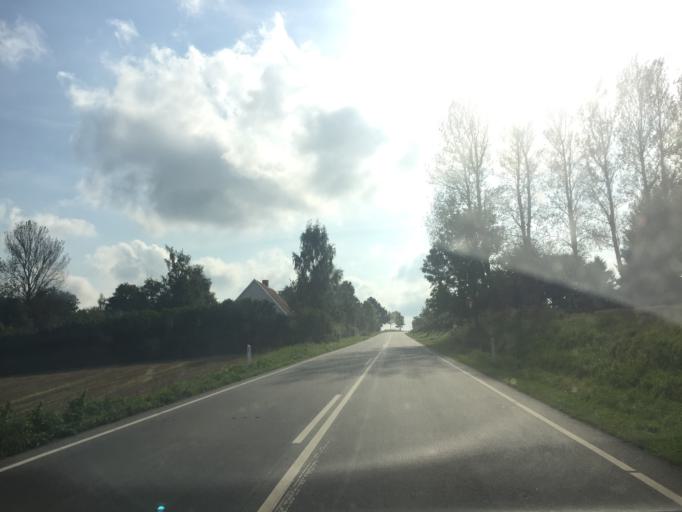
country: DK
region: Zealand
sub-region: Holbaek Kommune
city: Tollose
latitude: 55.6250
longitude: 11.7904
